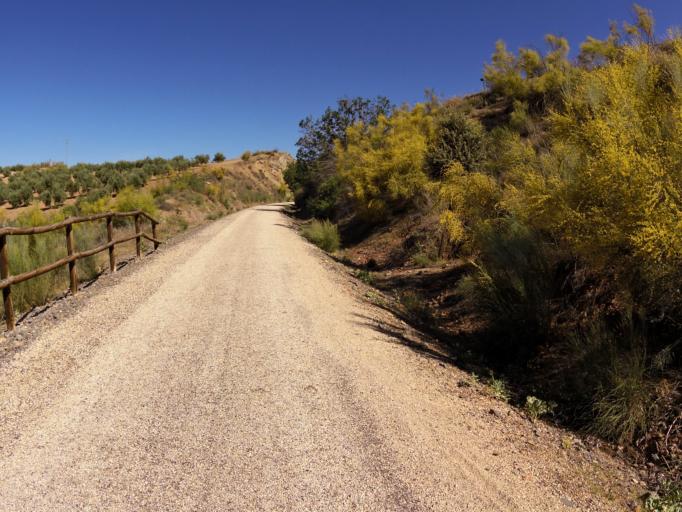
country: ES
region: Andalusia
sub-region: Provincia de Jaen
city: Alcaudete
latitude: 37.6008
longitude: -4.1579
